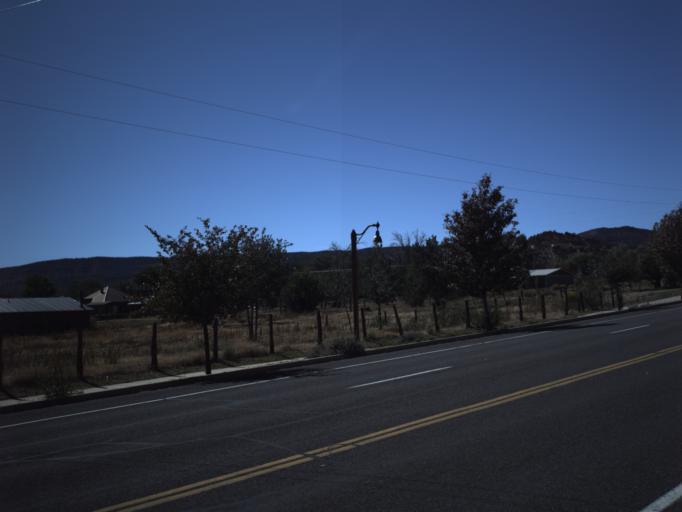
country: US
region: Utah
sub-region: Wayne County
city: Loa
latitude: 37.7704
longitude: -111.6051
